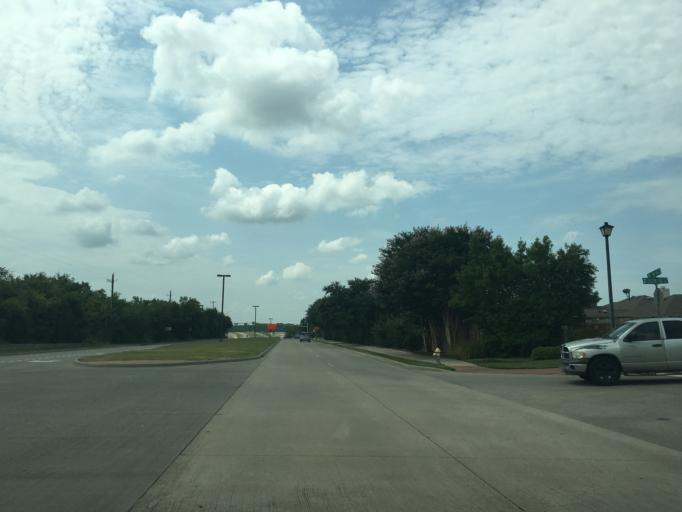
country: US
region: Texas
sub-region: Rockwall County
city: Rockwall
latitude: 32.9456
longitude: -96.4424
